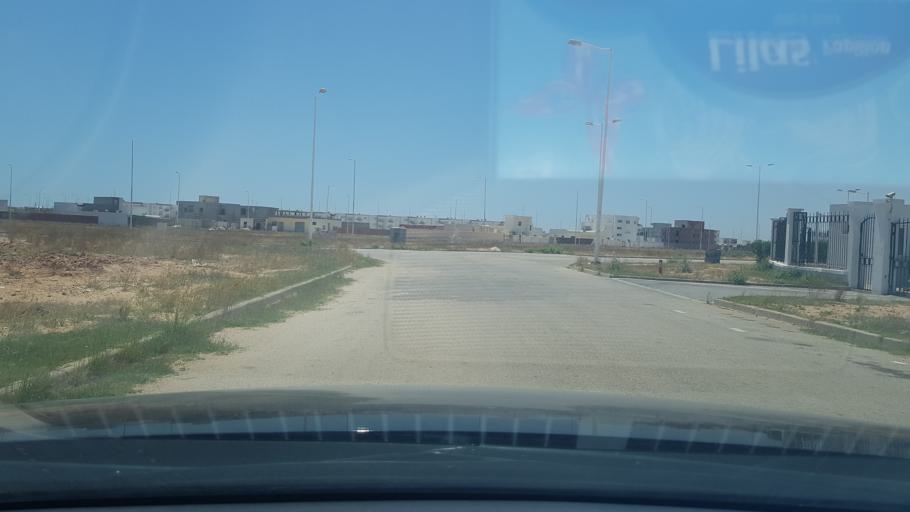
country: TN
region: Safaqis
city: Al Qarmadah
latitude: 34.8349
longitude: 10.7526
